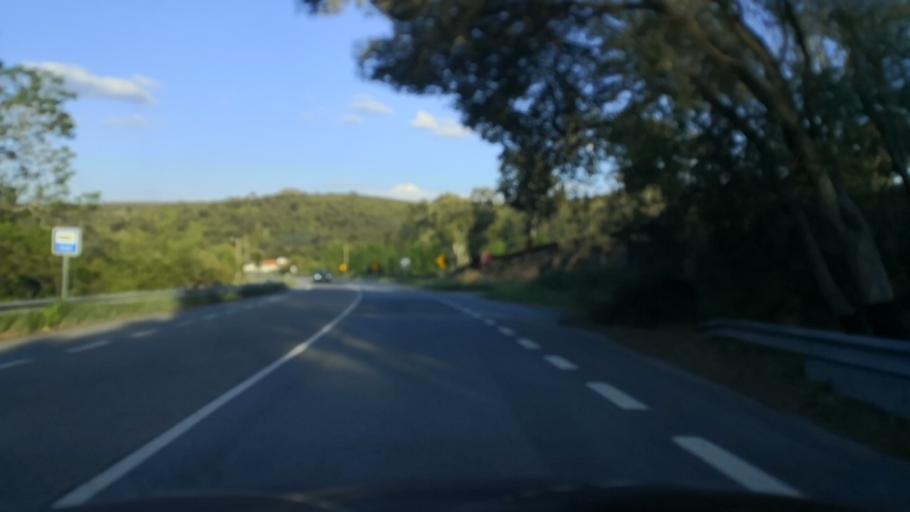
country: PT
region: Portalegre
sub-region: Portalegre
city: Sao Juliao
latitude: 39.3640
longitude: -7.3336
